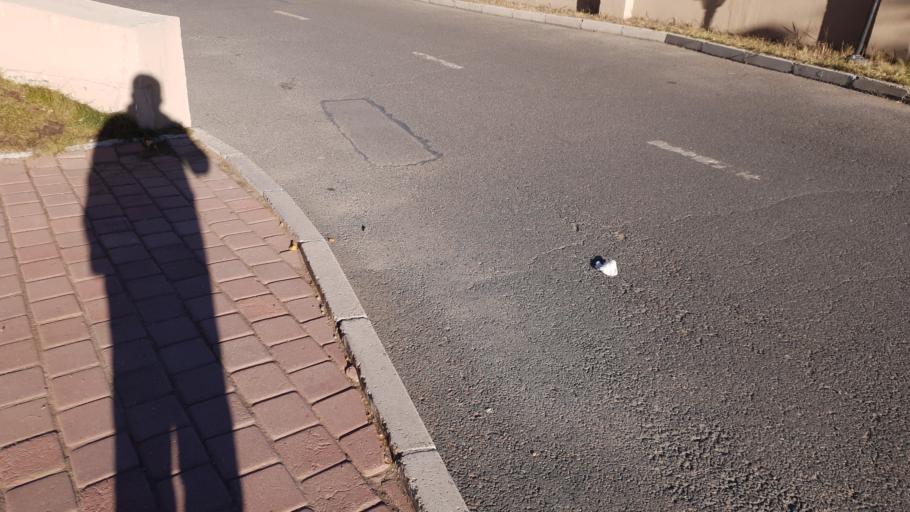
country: MN
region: Ulaanbaatar
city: Ulaanbaatar
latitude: 47.8810
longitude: 106.9155
